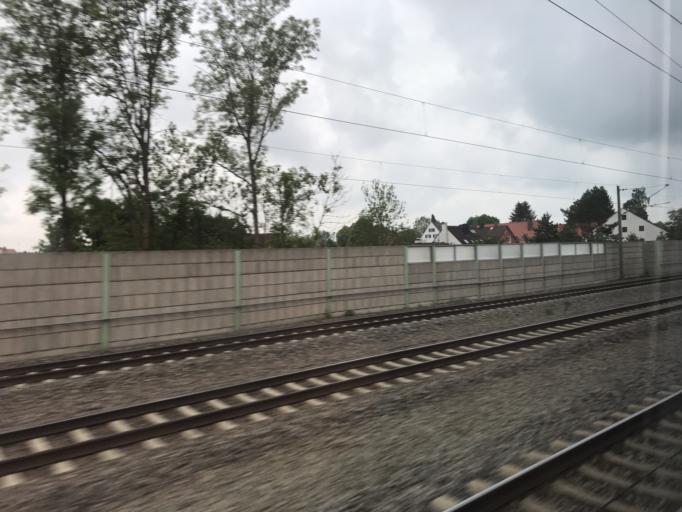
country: DE
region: Bavaria
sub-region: Upper Bavaria
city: Althegnenberg
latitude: 48.2351
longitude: 11.0669
